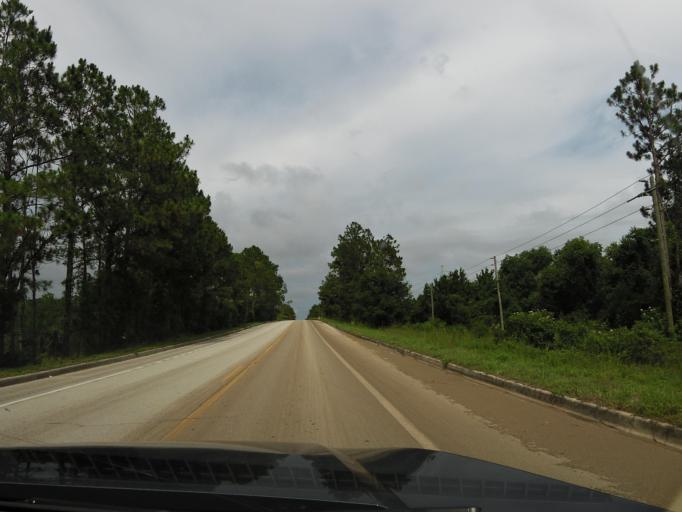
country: US
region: Florida
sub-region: Saint Johns County
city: Saint Augustine South
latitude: 29.8611
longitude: -81.3975
